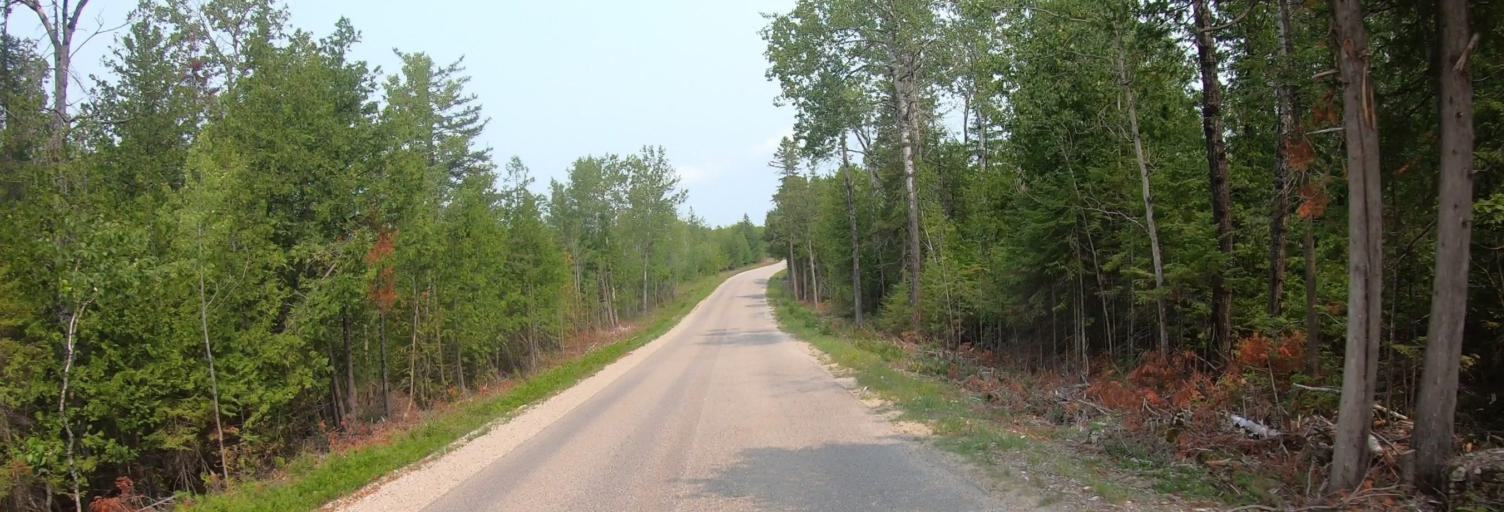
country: CA
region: Ontario
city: Thessalon
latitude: 46.0241
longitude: -83.6822
